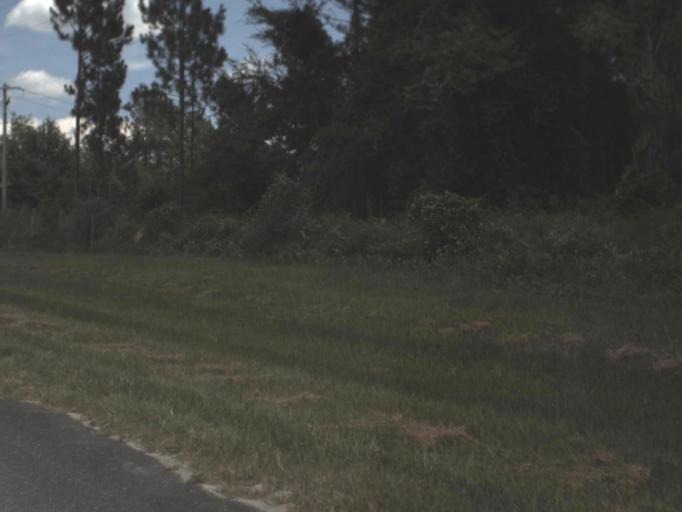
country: US
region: Florida
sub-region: Suwannee County
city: Wellborn
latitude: 30.0589
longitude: -82.7924
